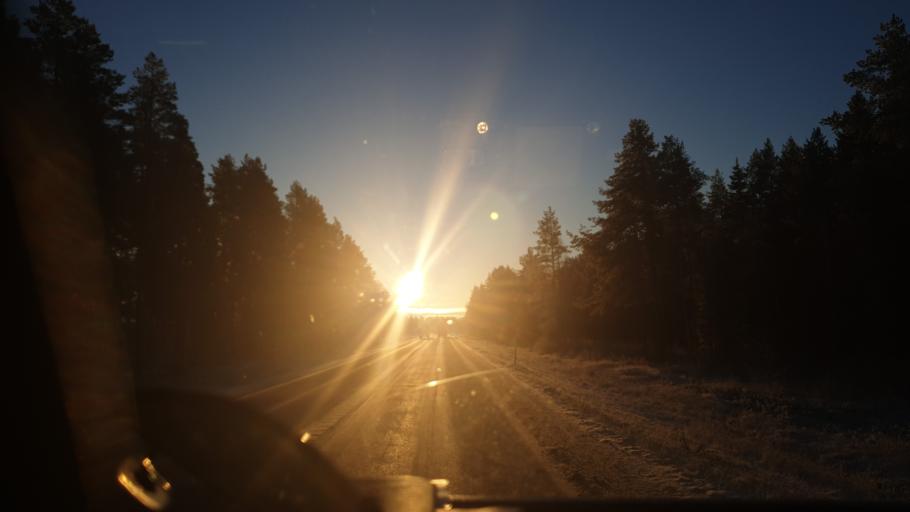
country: FI
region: Northern Ostrobothnia
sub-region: Ylivieska
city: Kalajoki
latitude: 64.2884
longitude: 23.9456
